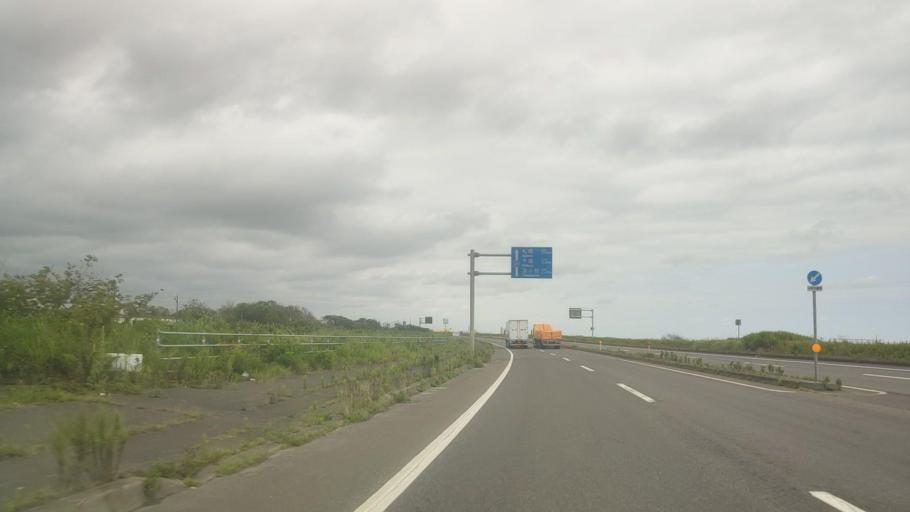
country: JP
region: Hokkaido
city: Shiraoi
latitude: 42.5387
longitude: 141.3381
